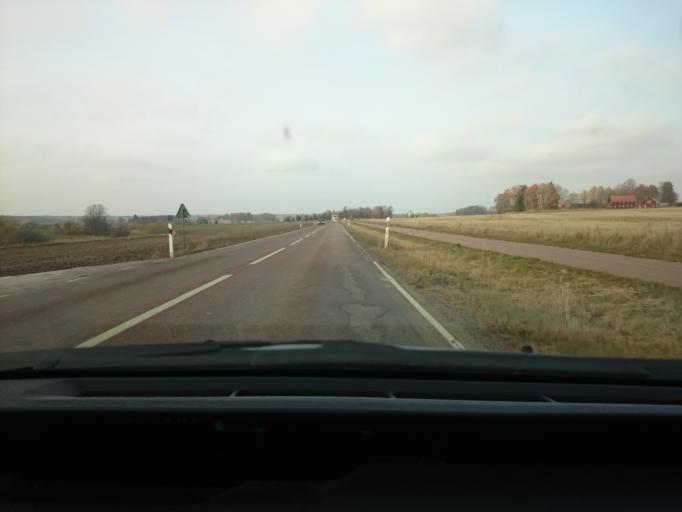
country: SE
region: Vaestmanland
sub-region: Vasteras
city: Skultuna
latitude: 59.6870
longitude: 16.4498
